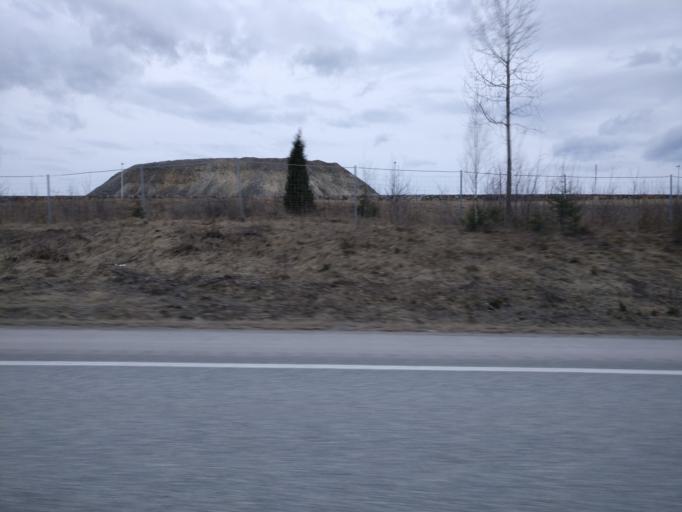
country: FI
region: Uusimaa
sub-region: Helsinki
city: Nurmijaervi
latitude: 60.4472
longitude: 24.8416
